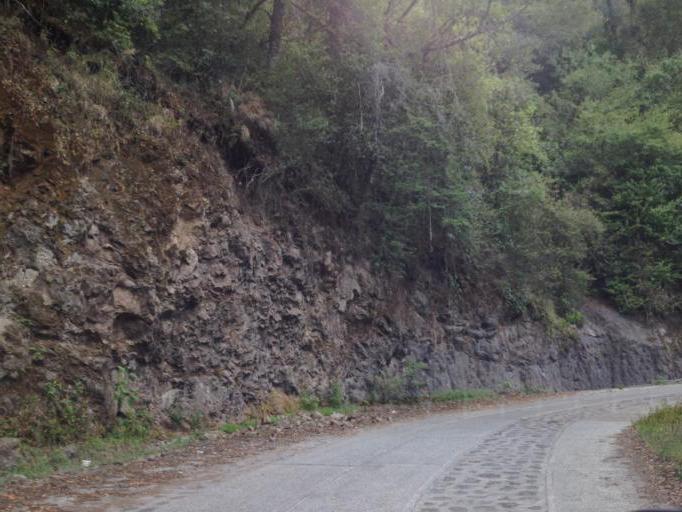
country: MX
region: Hidalgo
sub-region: Pachuca de Soto
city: San Miguel Cerezo (El Cerezo)
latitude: 20.2107
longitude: -98.6846
